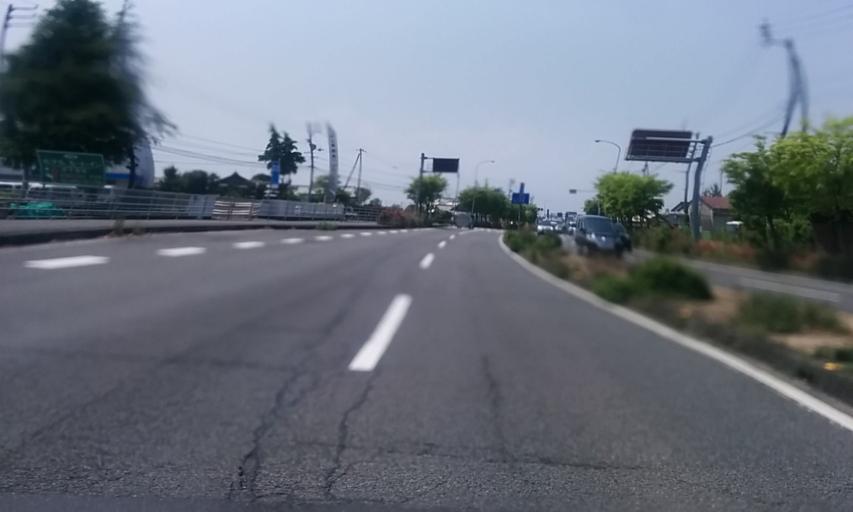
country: JP
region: Ehime
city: Saijo
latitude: 33.9196
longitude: 133.2397
